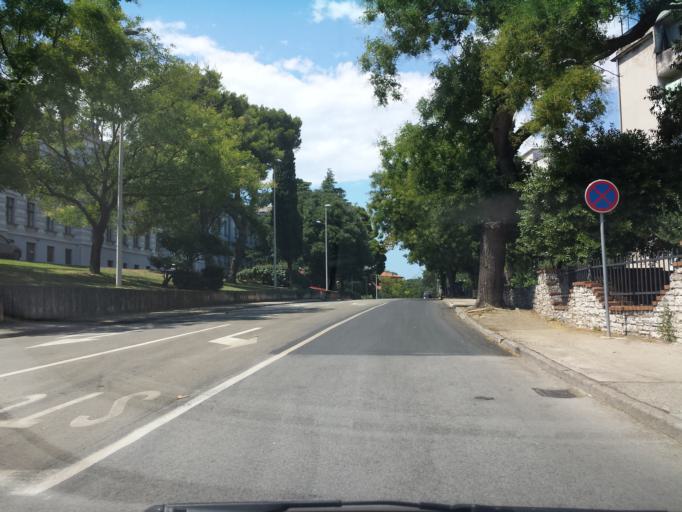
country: HR
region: Istarska
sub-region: Grad Pula
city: Pula
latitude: 44.8611
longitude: 13.8456
